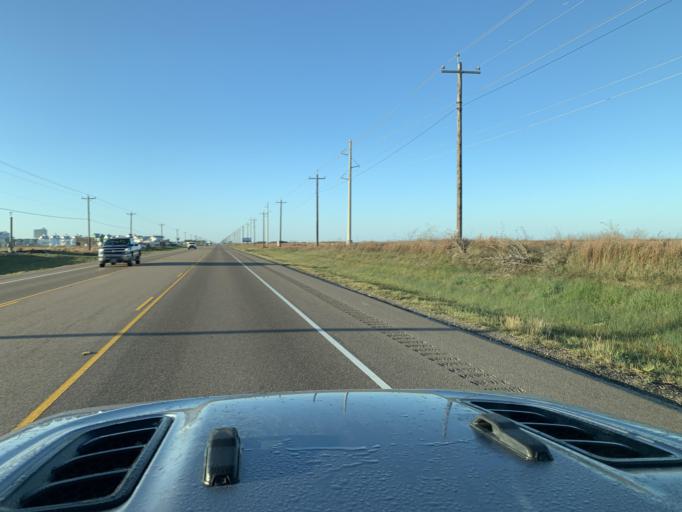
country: US
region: Texas
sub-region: Nueces County
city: Port Aransas
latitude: 27.7601
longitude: -97.1179
